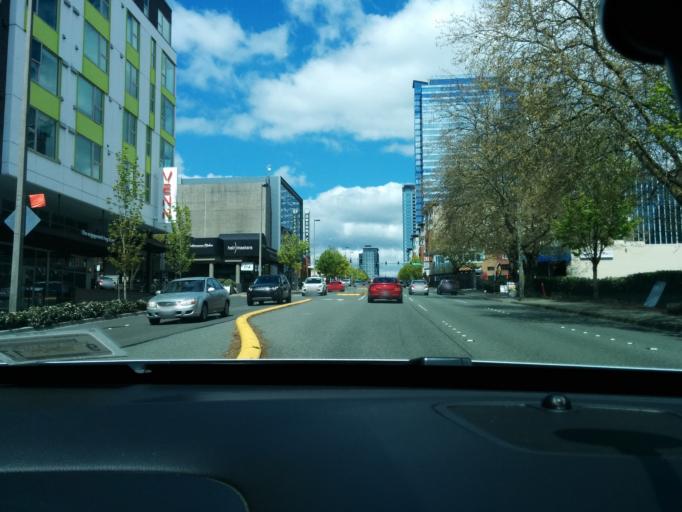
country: US
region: Washington
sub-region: King County
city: Bellevue
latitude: 47.6107
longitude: -122.2015
